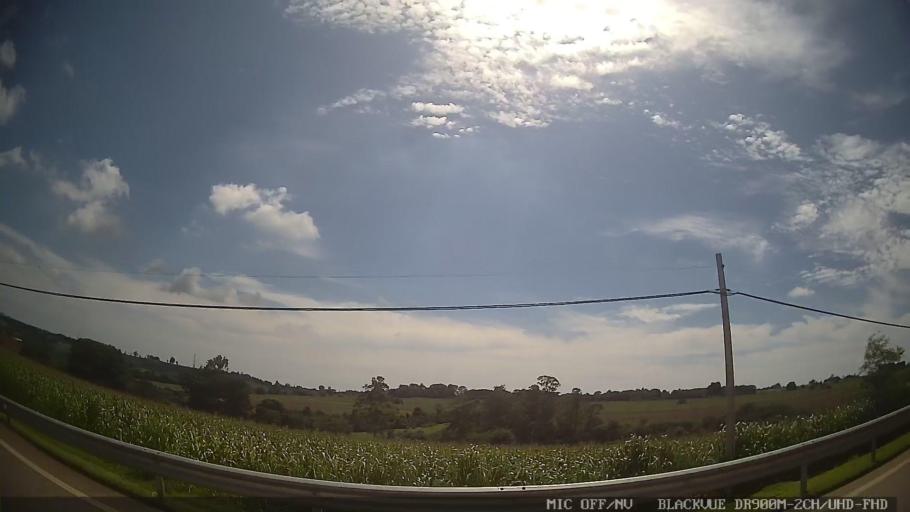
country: BR
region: Sao Paulo
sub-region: Tiete
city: Tiete
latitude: -23.1230
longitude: -47.6995
